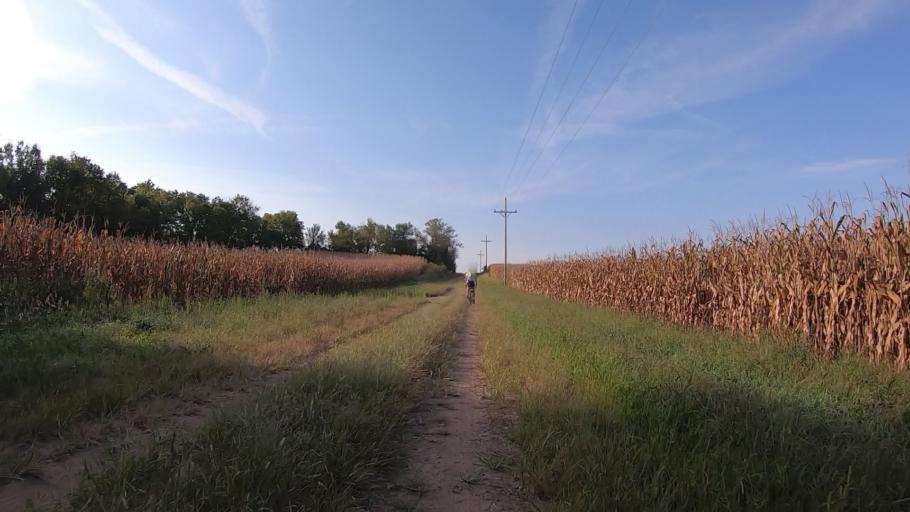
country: US
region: Kansas
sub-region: Marshall County
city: Blue Rapids
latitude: 39.7107
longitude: -96.7793
